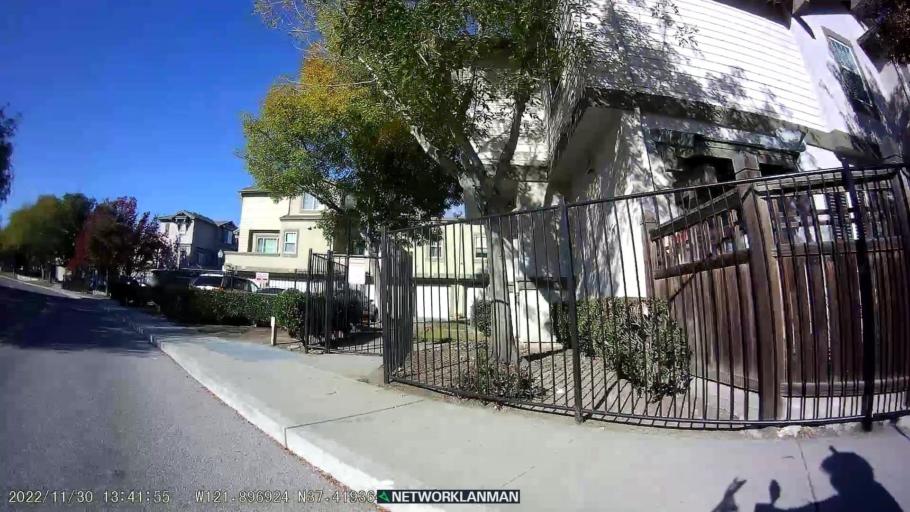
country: US
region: California
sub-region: Santa Clara County
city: Milpitas
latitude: 37.4194
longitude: -121.8970
